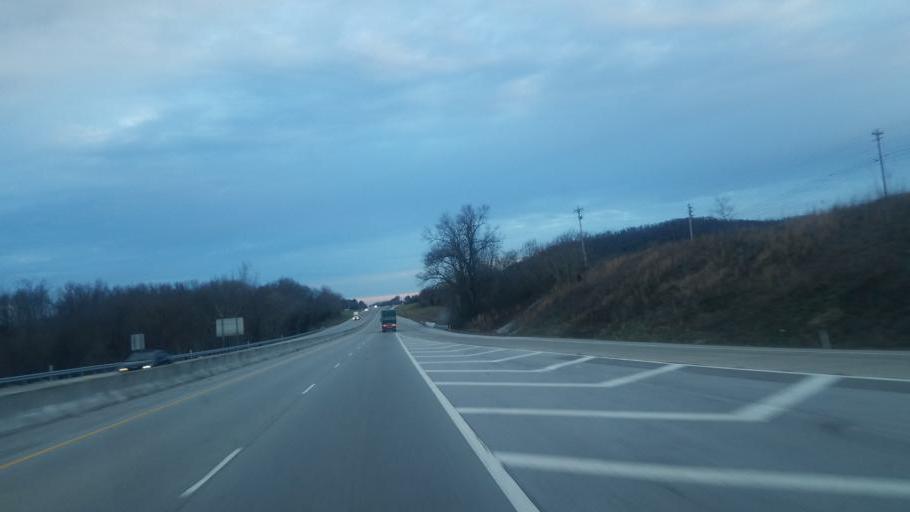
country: US
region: Tennessee
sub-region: White County
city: Sparta
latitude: 35.9923
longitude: -85.5013
